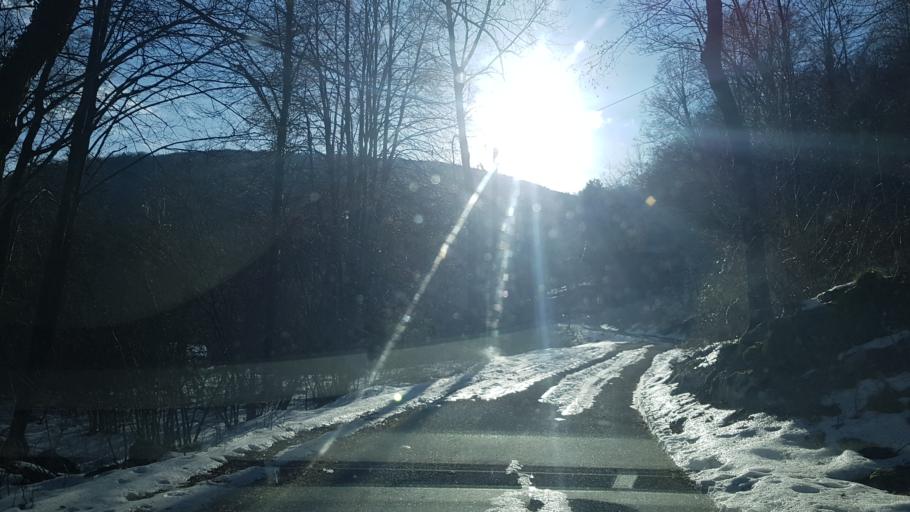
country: IT
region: Friuli Venezia Giulia
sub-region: Provincia di Udine
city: Trasaghis
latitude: 46.2927
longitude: 13.0282
